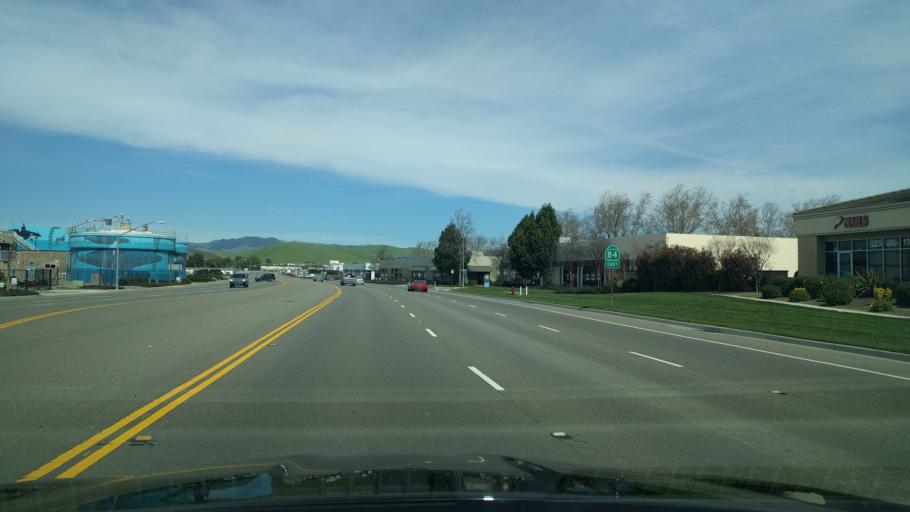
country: US
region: California
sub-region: Alameda County
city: Livermore
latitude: 37.6896
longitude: -121.8058
